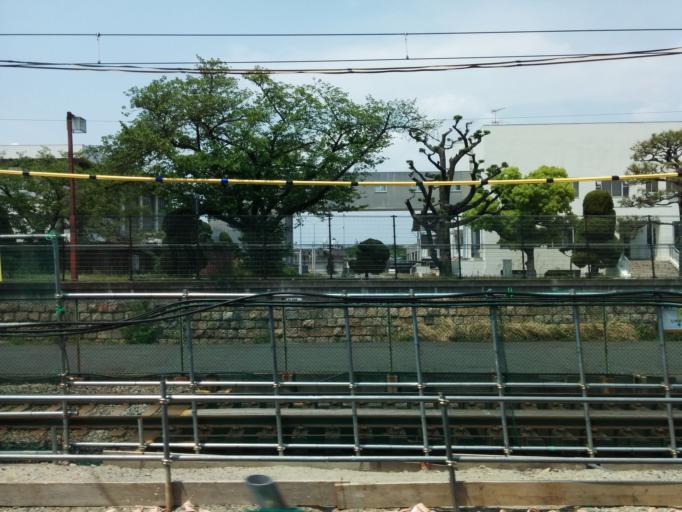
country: JP
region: Osaka
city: Suita
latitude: 34.7335
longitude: 135.5156
